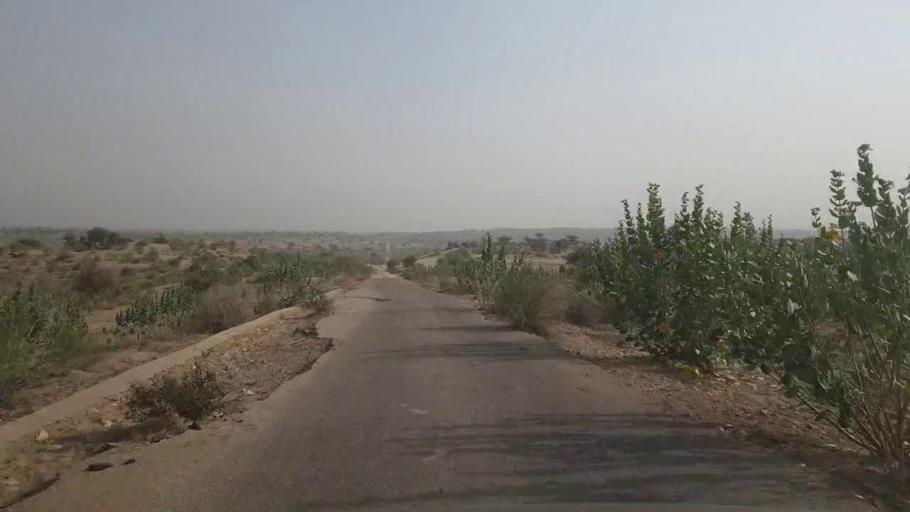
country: PK
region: Sindh
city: Chor
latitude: 25.5252
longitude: 69.9618
